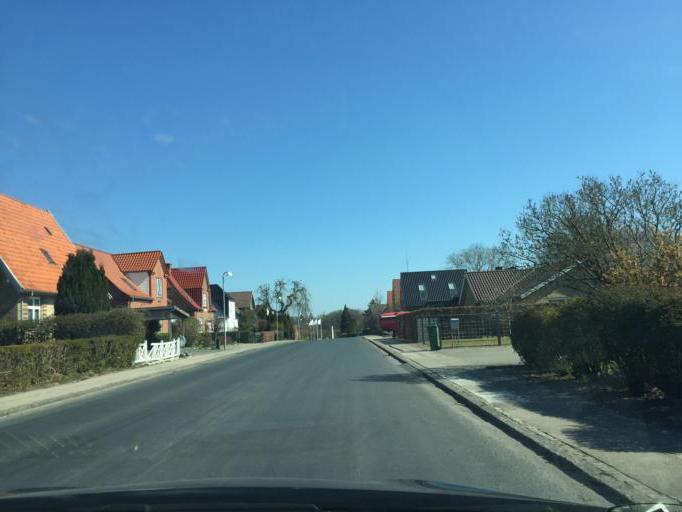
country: DK
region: South Denmark
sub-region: Faaborg-Midtfyn Kommune
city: Ringe
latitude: 55.2410
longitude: 10.4835
